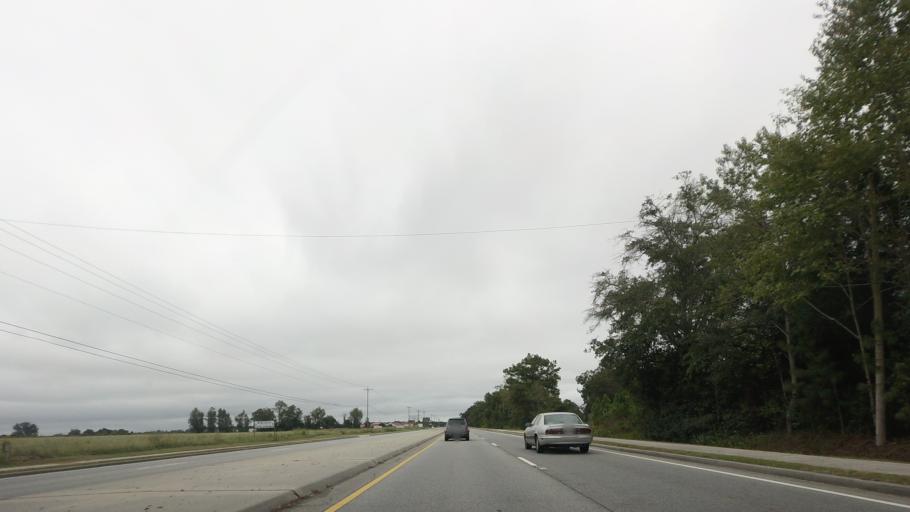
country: US
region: Georgia
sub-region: Berrien County
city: Ray City
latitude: 30.9551
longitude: -83.2260
